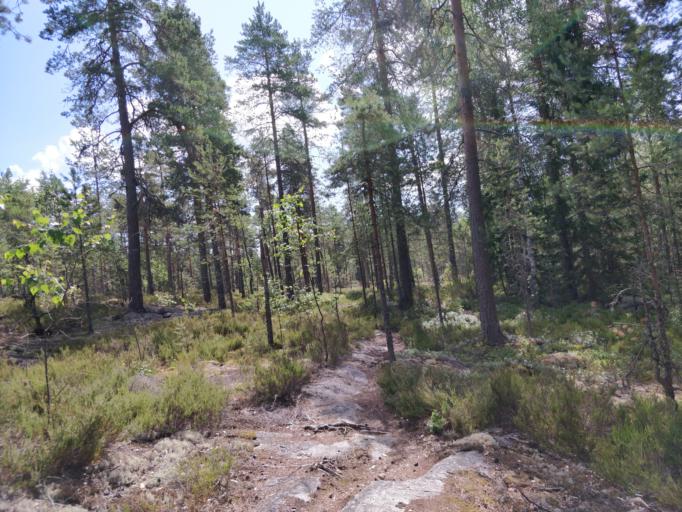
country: FI
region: Uusimaa
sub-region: Helsinki
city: Vihti
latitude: 60.3127
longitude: 24.4717
